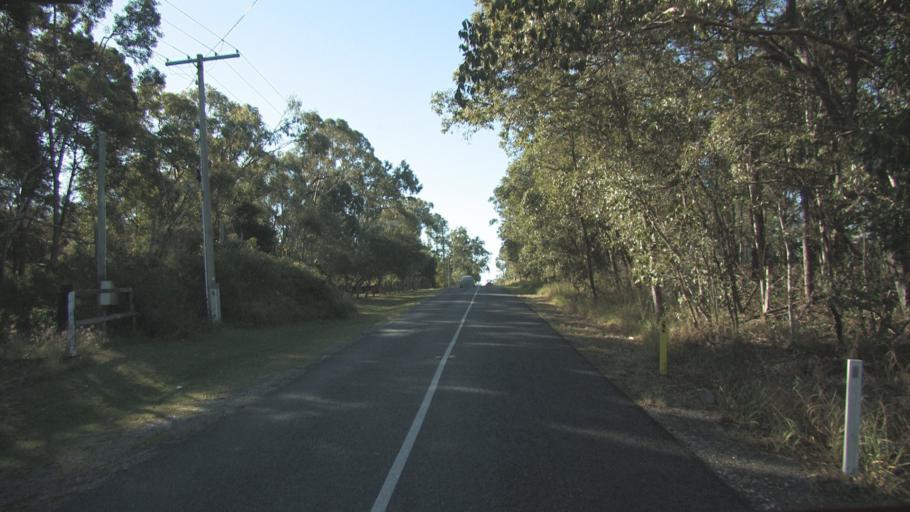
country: AU
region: Queensland
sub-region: Logan
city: Logan Reserve
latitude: -27.7290
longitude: 153.1047
